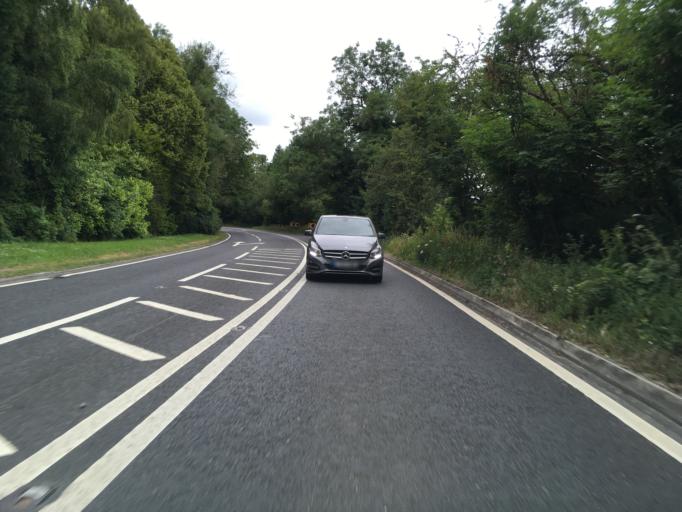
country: GB
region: England
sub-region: Gloucestershire
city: Shipton Village
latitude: 51.8831
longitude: -1.9806
